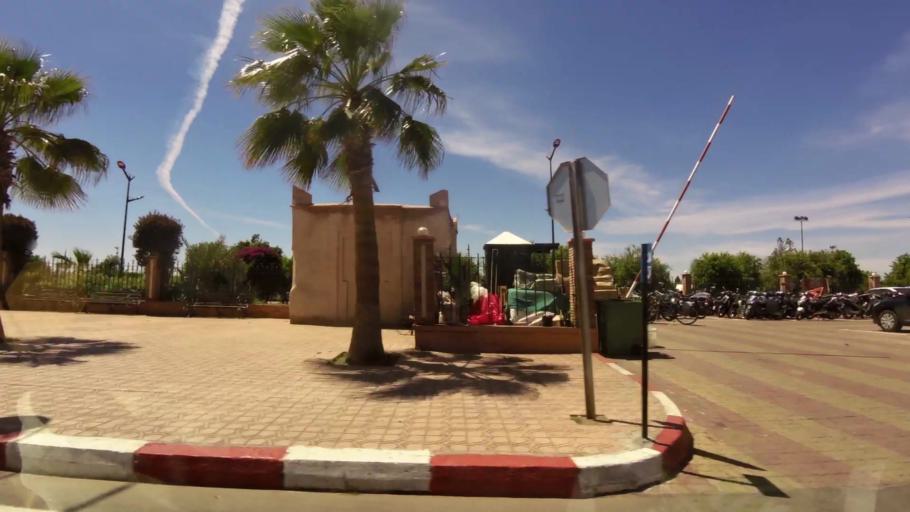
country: MA
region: Marrakech-Tensift-Al Haouz
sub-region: Marrakech
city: Marrakesh
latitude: 31.6124
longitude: -7.9896
